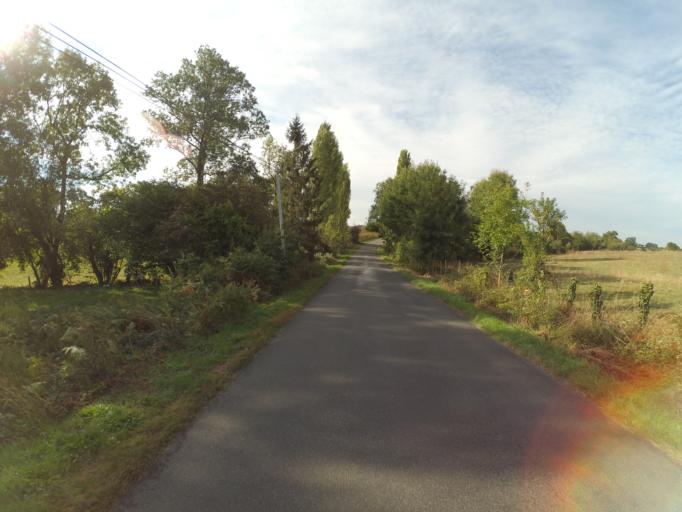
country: FR
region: Pays de la Loire
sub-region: Departement de Maine-et-Loire
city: Saint-Crespin-sur-Moine
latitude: 47.1304
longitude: -1.1960
